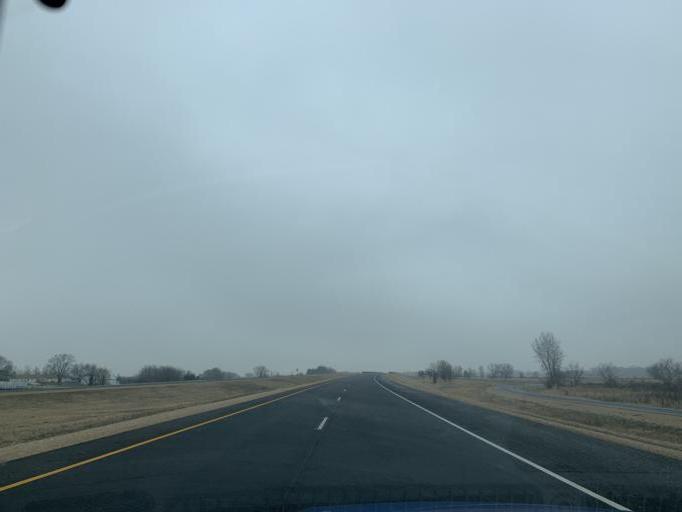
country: US
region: Wisconsin
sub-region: Dane County
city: Sun Prairie
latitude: 43.2373
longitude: -89.1495
